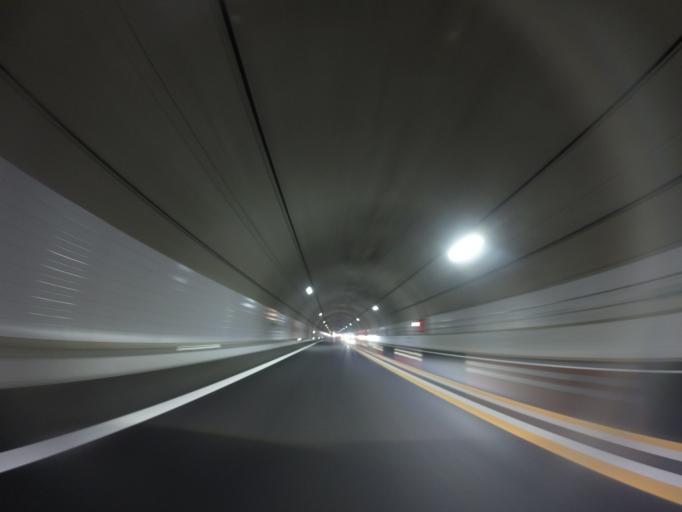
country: JP
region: Yamanashi
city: Ryuo
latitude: 35.4332
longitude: 138.4580
